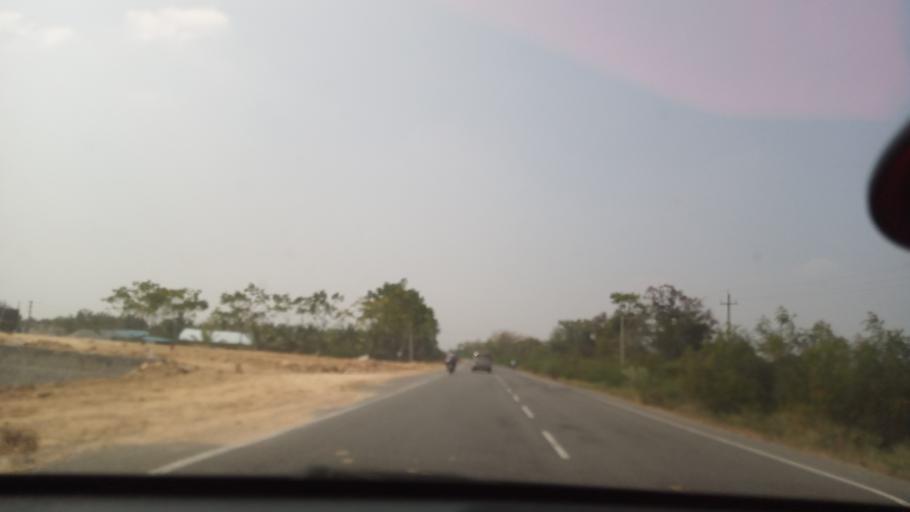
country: IN
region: Karnataka
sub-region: Mysore
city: Nanjangud
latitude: 12.0613
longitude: 76.7607
